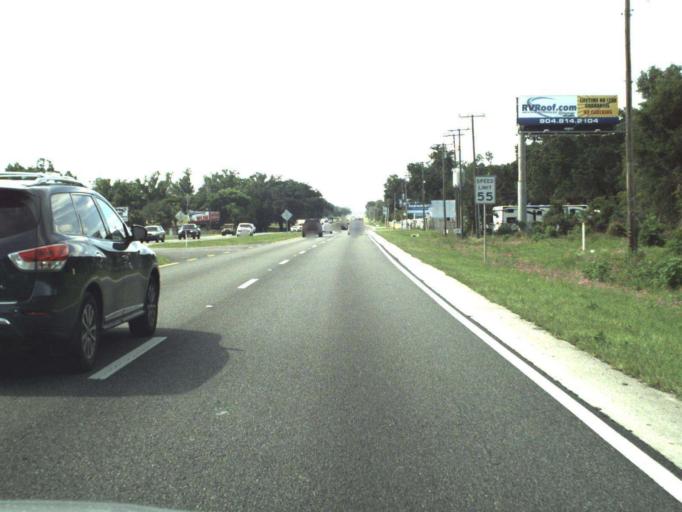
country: US
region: Florida
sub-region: Marion County
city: Belleview
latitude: 29.1074
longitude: -82.0920
